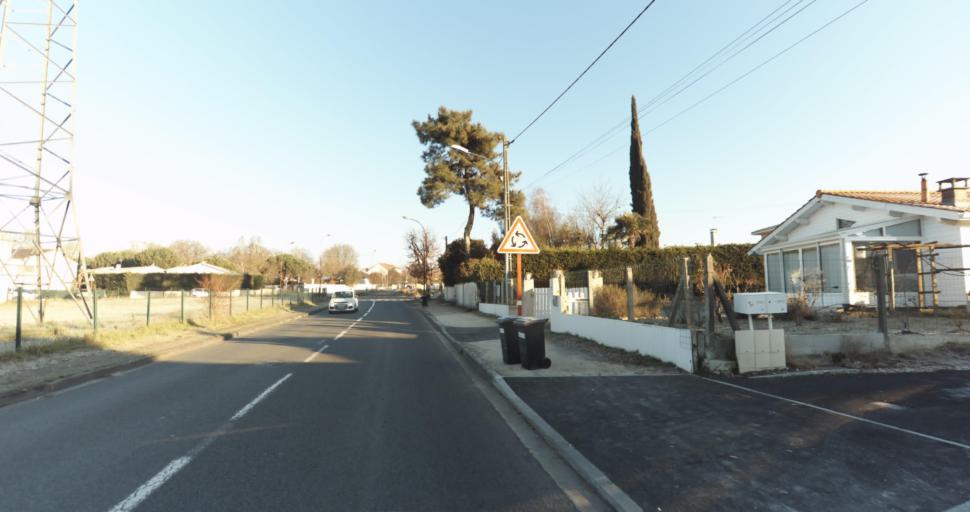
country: FR
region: Aquitaine
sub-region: Departement de la Gironde
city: Carbon-Blanc
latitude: 44.9068
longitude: -0.5032
